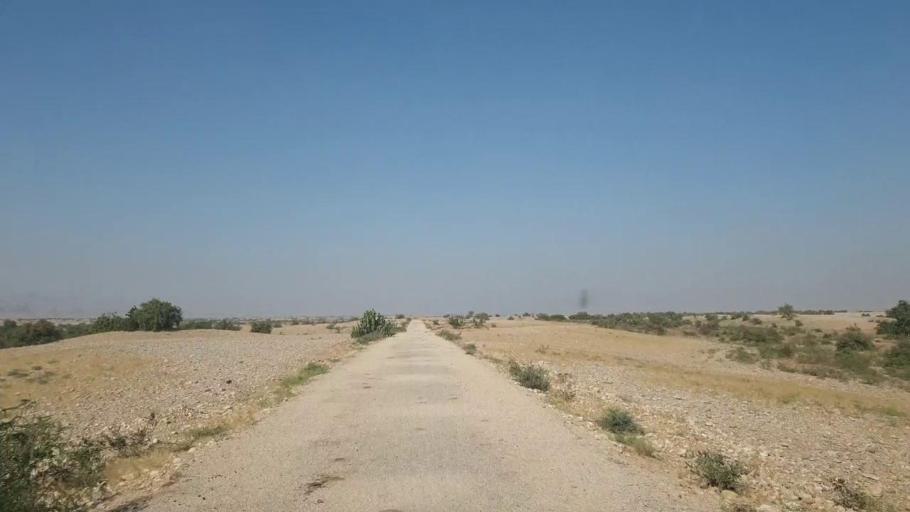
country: PK
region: Sindh
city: Jamshoro
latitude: 25.4862
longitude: 67.8398
